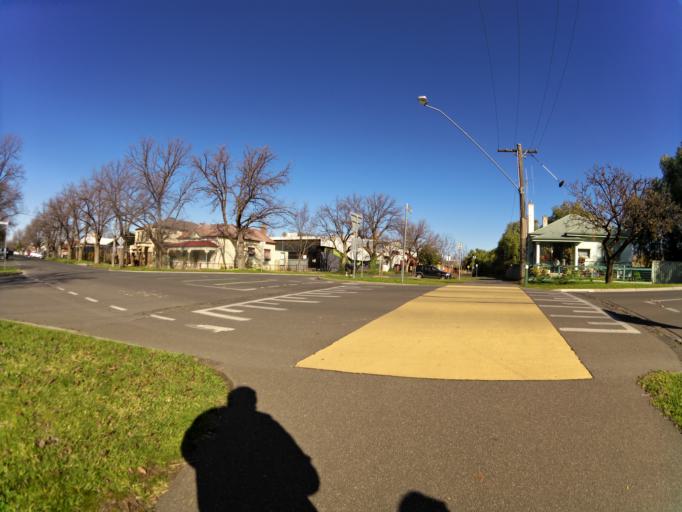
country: AU
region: Victoria
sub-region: Greater Bendigo
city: Bendigo
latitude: -36.7531
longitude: 144.2851
